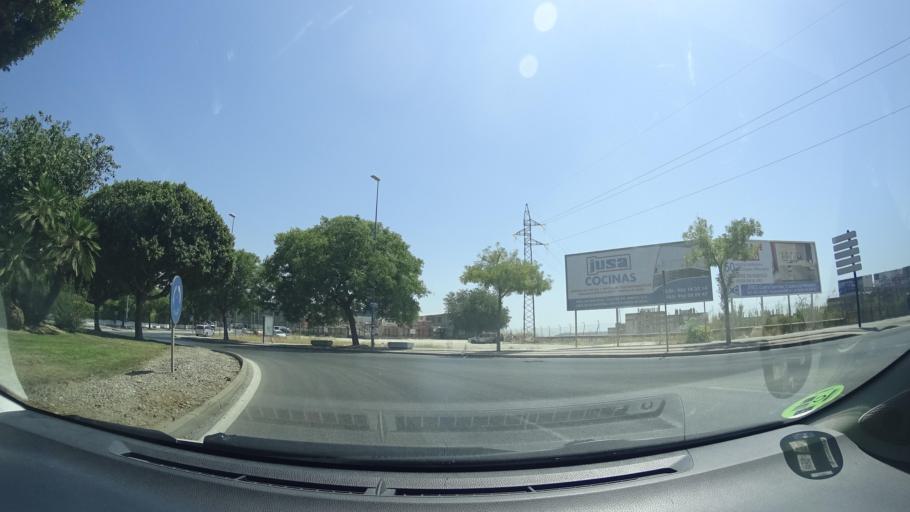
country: ES
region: Andalusia
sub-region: Provincia de Cadiz
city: Jerez de la Frontera
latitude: 36.6732
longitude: -6.1225
